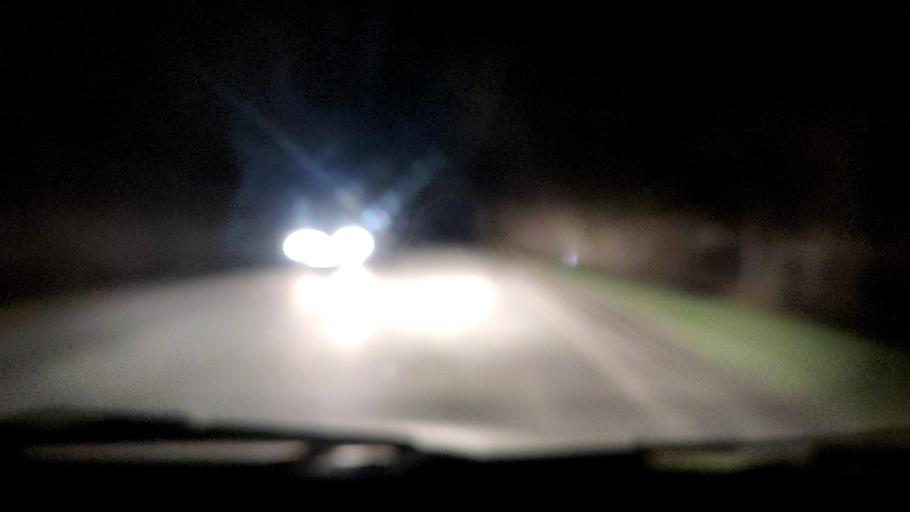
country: RU
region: Voronezj
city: Podkletnoye
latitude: 51.6264
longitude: 39.5332
